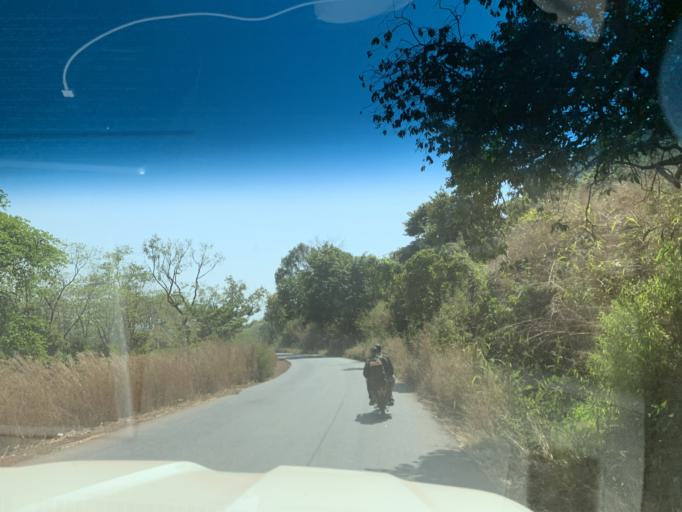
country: GN
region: Kindia
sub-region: Kindia
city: Kindia
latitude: 10.0087
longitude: -12.8023
